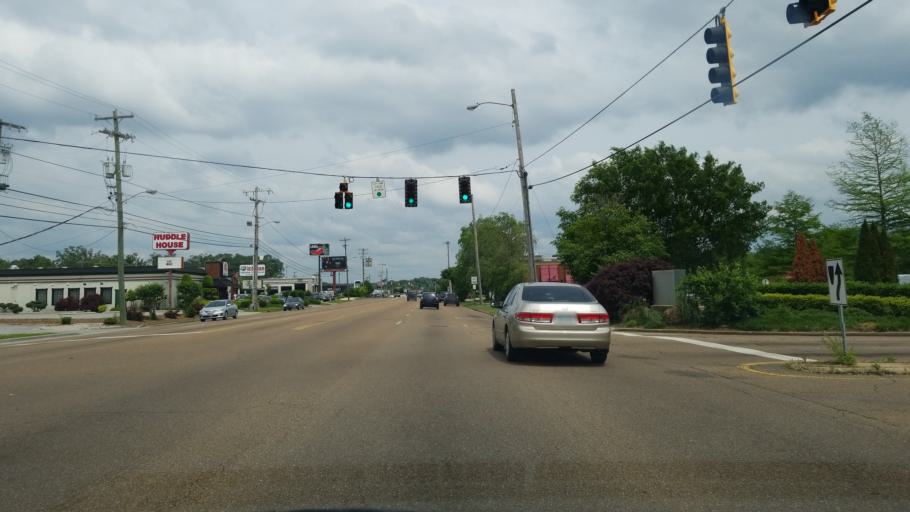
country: US
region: Tennessee
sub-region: Hamilton County
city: East Ridge
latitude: 35.0105
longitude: -85.2176
